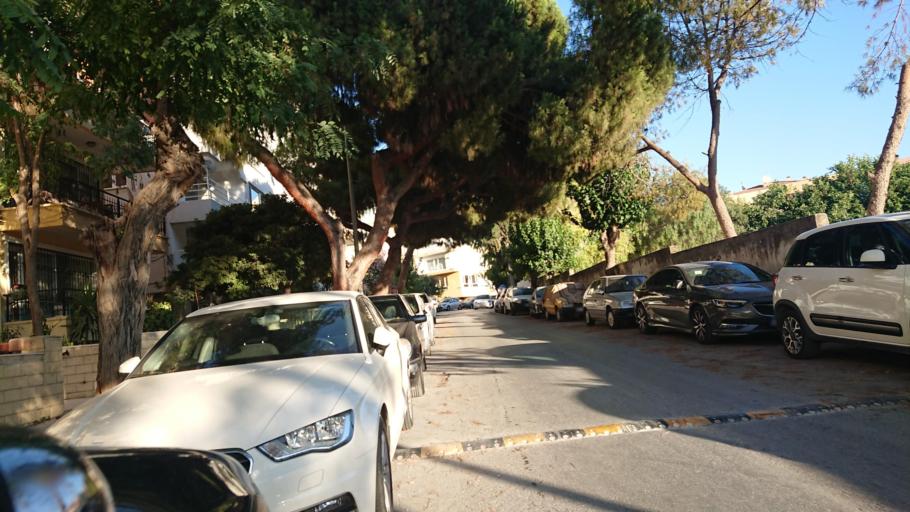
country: TR
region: Aydin
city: Kusadasi
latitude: 37.8641
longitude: 27.2641
